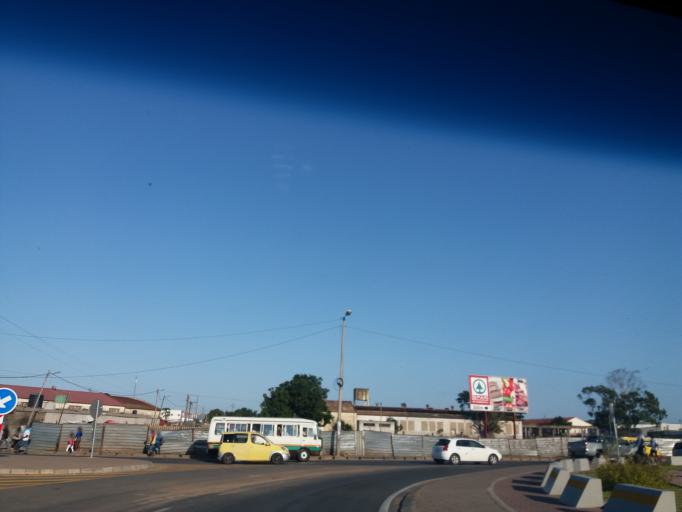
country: MZ
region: Maputo City
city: Maputo
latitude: -25.9342
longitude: 32.5505
